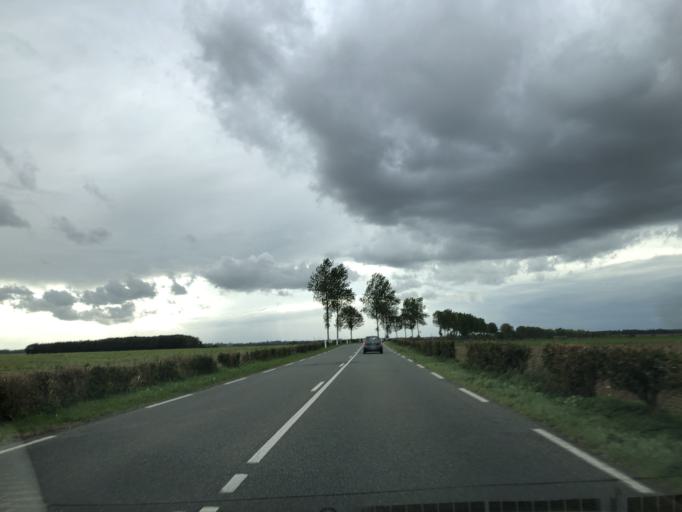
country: FR
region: Picardie
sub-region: Departement de la Somme
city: Abbeville
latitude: 50.0990
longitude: 1.7470
